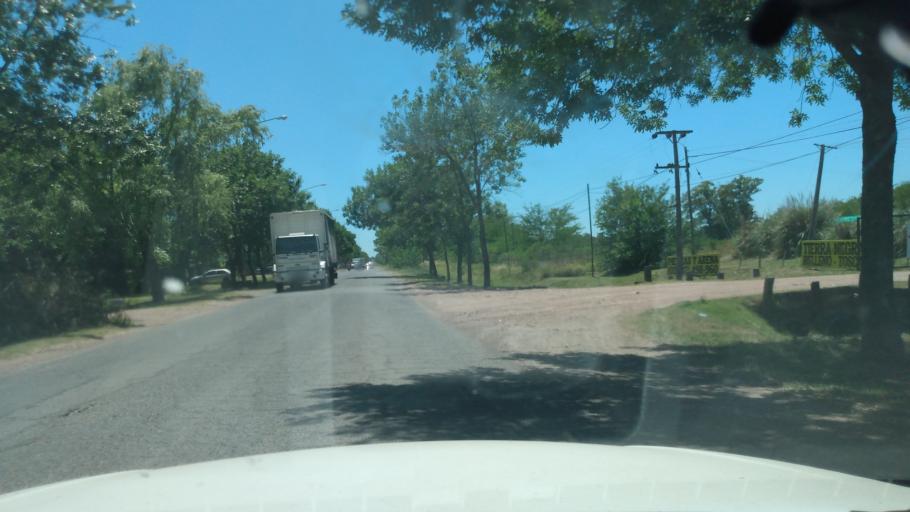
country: AR
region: Buenos Aires
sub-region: Partido de Lujan
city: Lujan
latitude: -34.5799
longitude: -59.1716
